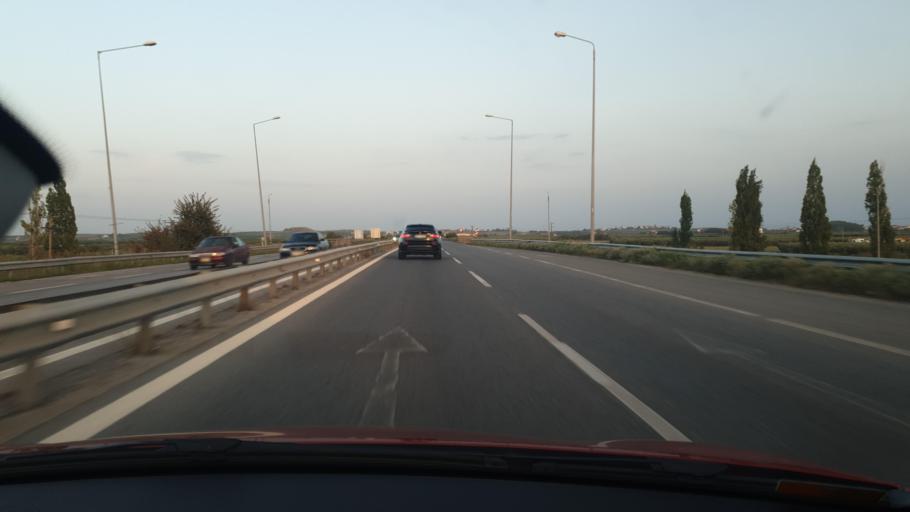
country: GR
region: Central Macedonia
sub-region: Nomos Chalkidikis
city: Nea Plagia
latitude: 40.2815
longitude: 23.1922
